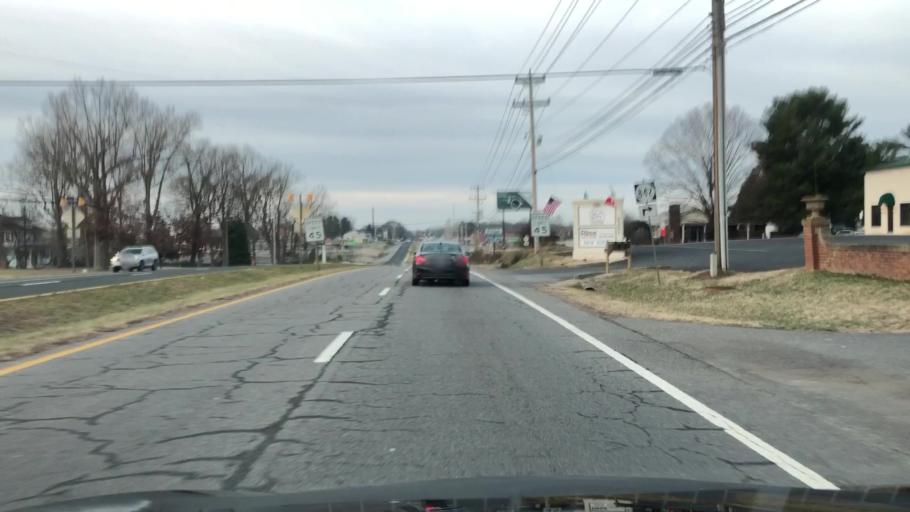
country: US
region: Virginia
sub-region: Campbell County
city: Timberlake
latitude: 37.3260
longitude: -79.2509
